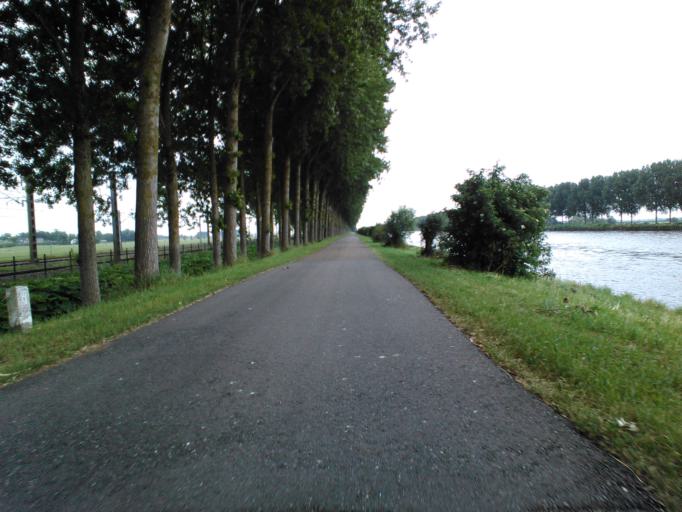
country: NL
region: Utrecht
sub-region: Stichtse Vecht
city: Vreeland
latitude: 52.2334
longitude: 5.0078
